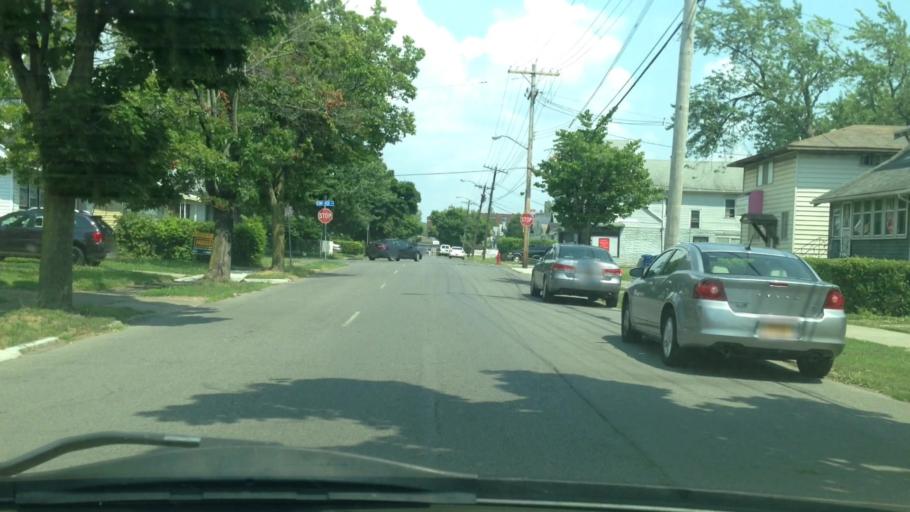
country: US
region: New York
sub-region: Erie County
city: Eggertsville
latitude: 42.9402
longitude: -78.8181
